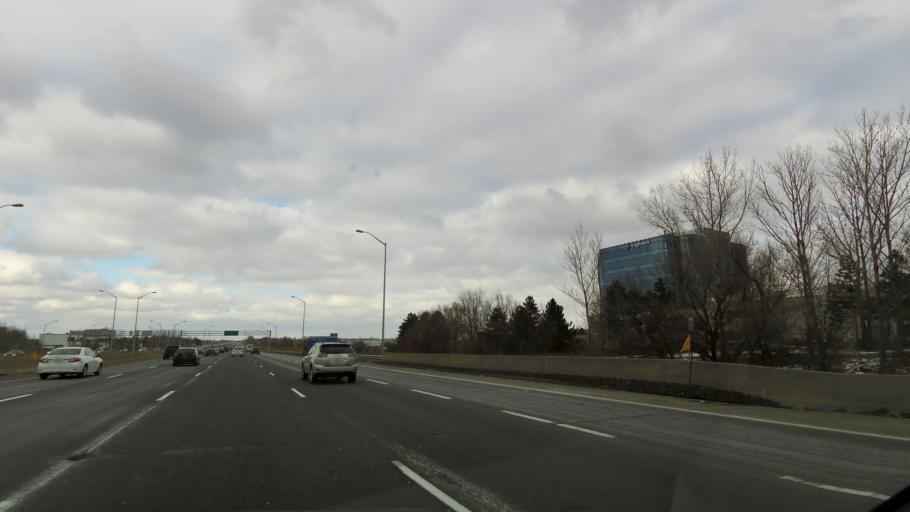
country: CA
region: Ontario
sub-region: York
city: Richmond Hill
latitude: 43.8539
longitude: -79.3724
